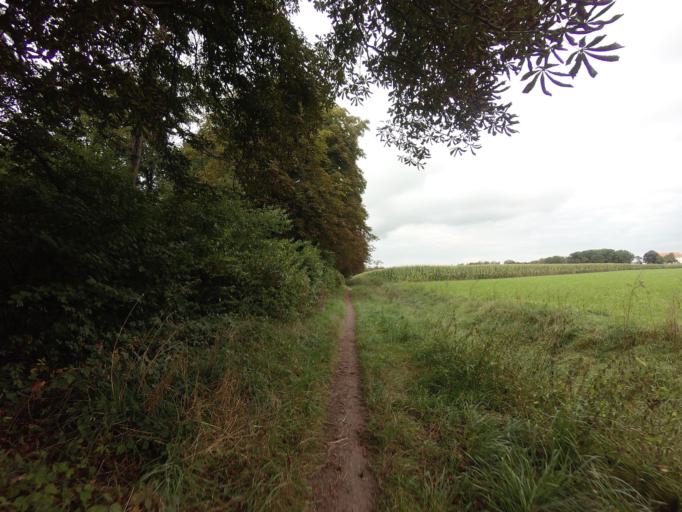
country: NL
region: Overijssel
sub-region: Gemeente Losser
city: Losser
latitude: 52.2612
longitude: 7.0393
